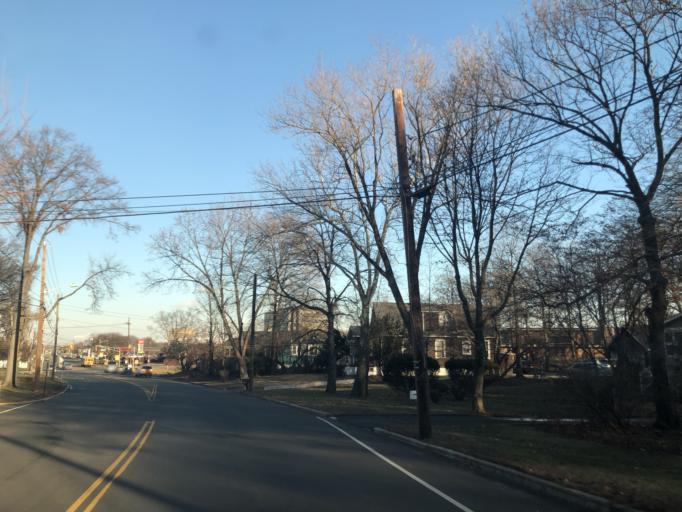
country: US
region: New Jersey
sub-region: Middlesex County
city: Fords
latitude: 40.5427
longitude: -74.3056
